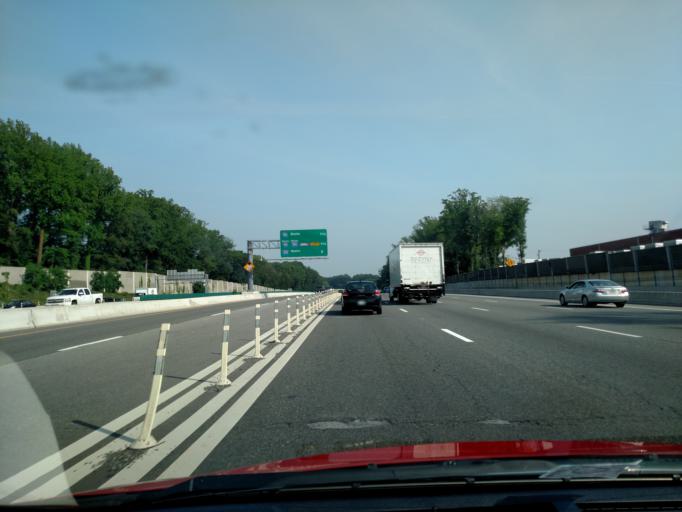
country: US
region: Virginia
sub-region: Fairfax County
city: Ravensworth
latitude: 38.8096
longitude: -77.2168
